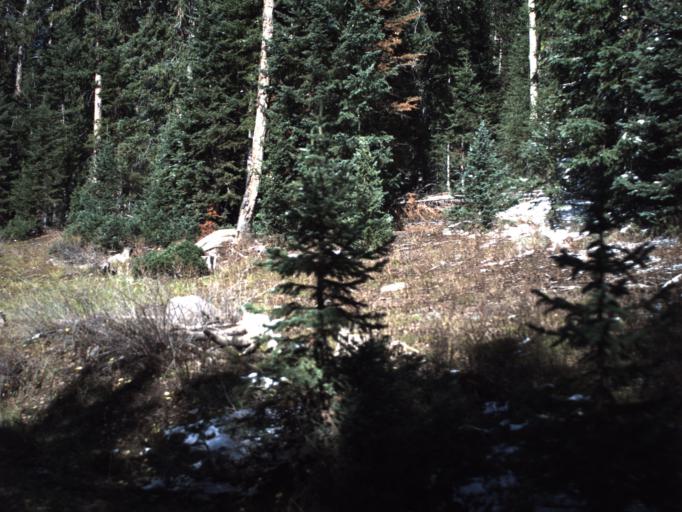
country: US
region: Utah
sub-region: Piute County
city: Junction
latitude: 38.2905
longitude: -112.3591
